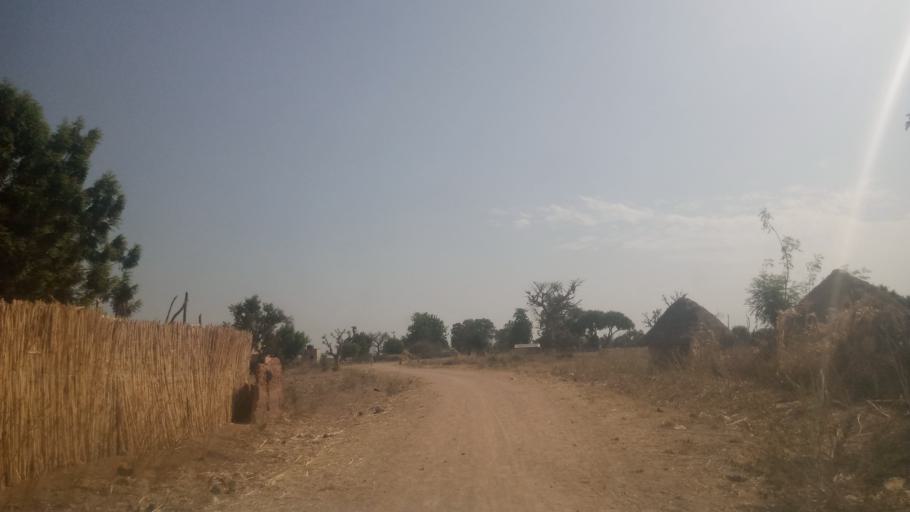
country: NG
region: Adamawa
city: Mayo Belwa
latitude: 9.0792
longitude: 12.0354
